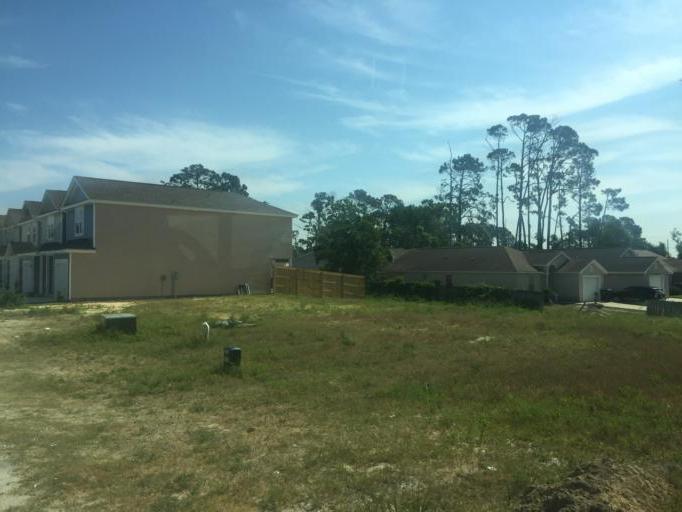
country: US
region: Florida
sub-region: Bay County
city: Lower Grand Lagoon
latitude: 30.1589
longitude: -85.7576
